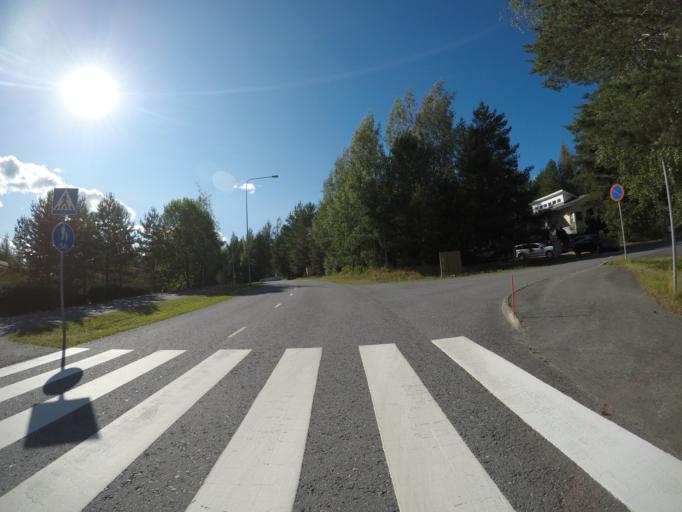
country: FI
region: Haeme
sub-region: Haemeenlinna
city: Haemeenlinna
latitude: 61.0221
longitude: 24.5181
